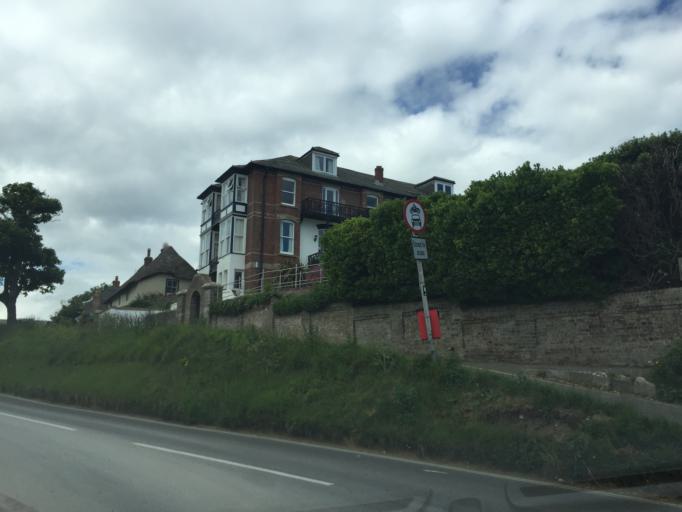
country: GB
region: England
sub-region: Dorset
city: Wool
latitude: 50.6203
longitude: -2.2530
